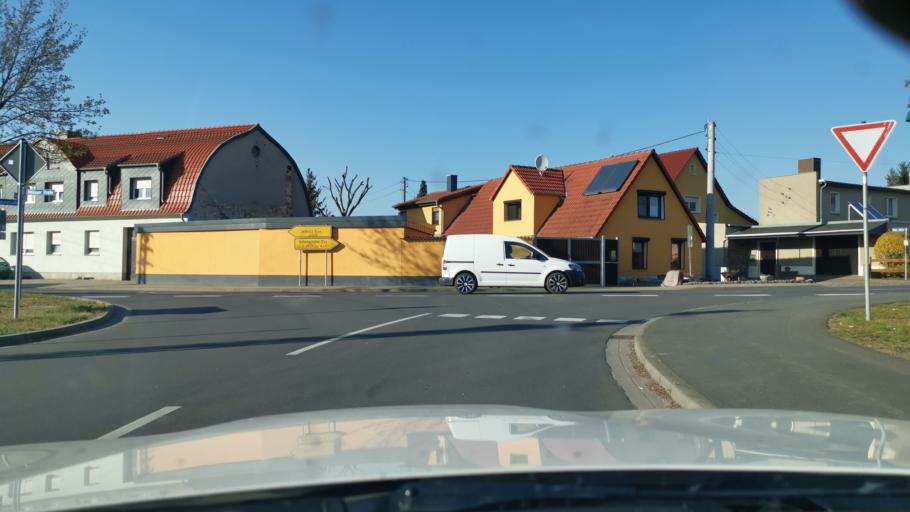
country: DE
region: Saxony-Anhalt
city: Jessnitz
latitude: 51.7124
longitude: 12.3088
